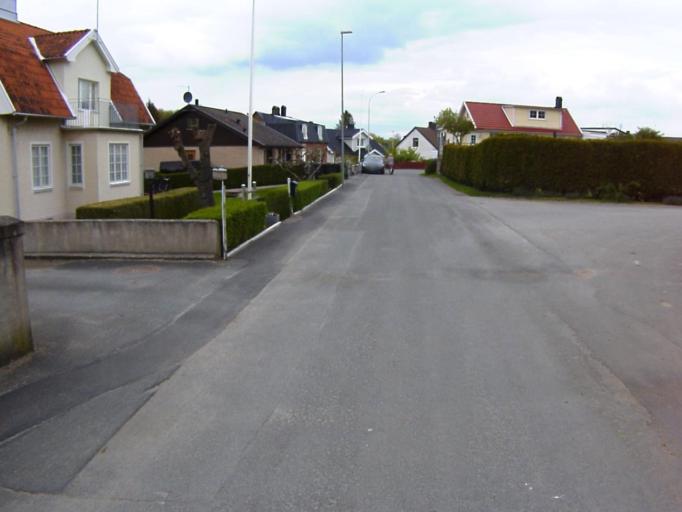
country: SE
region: Skane
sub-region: Kristianstads Kommun
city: Kristianstad
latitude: 56.0156
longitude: 14.1903
